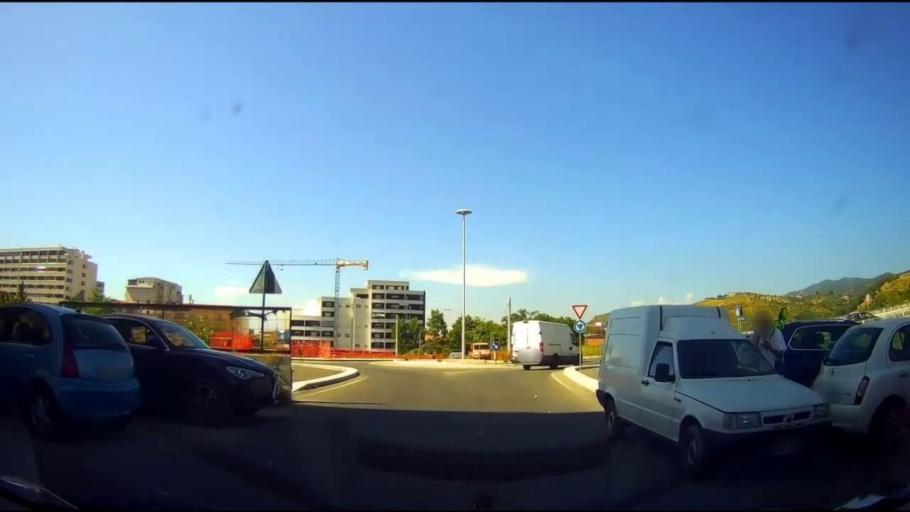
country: IT
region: Calabria
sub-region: Provincia di Cosenza
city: Cosenza
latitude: 39.2977
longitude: 16.2583
